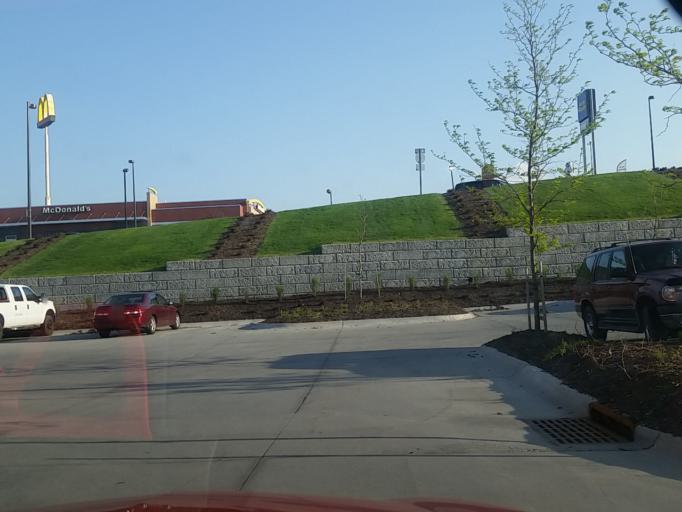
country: US
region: Nebraska
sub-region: Sarpy County
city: Gretna
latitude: 41.0982
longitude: -96.2521
